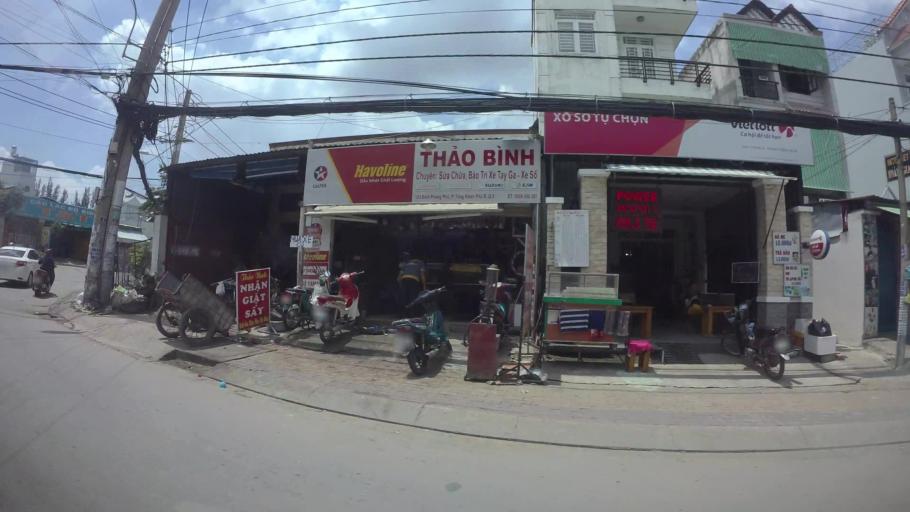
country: VN
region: Ho Chi Minh City
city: Quan Chin
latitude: 10.8377
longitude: 106.7810
